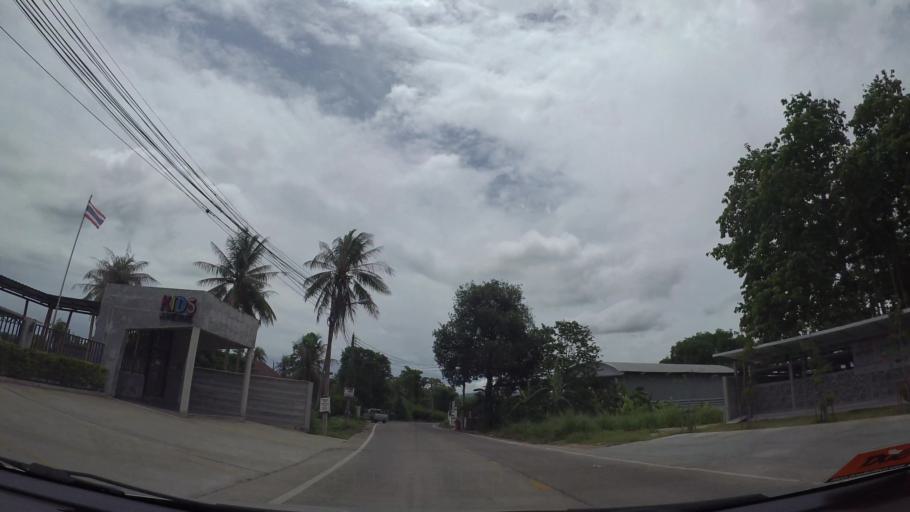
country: TH
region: Chon Buri
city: Si Racha
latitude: 13.1714
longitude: 100.9763
